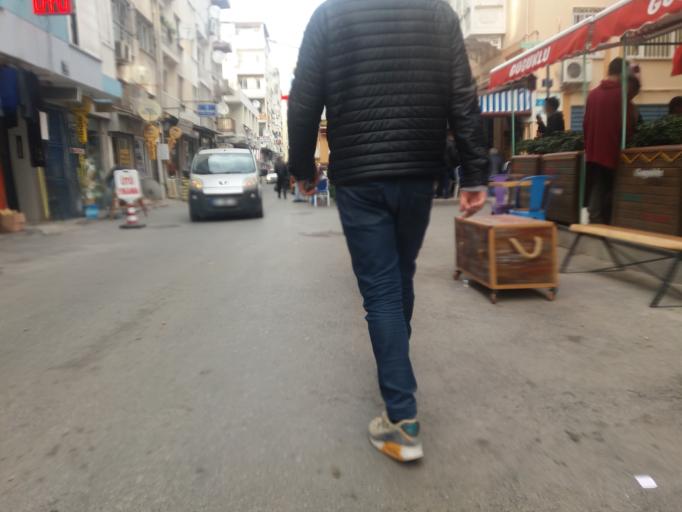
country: TR
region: Izmir
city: Izmir
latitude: 38.4373
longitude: 27.1447
